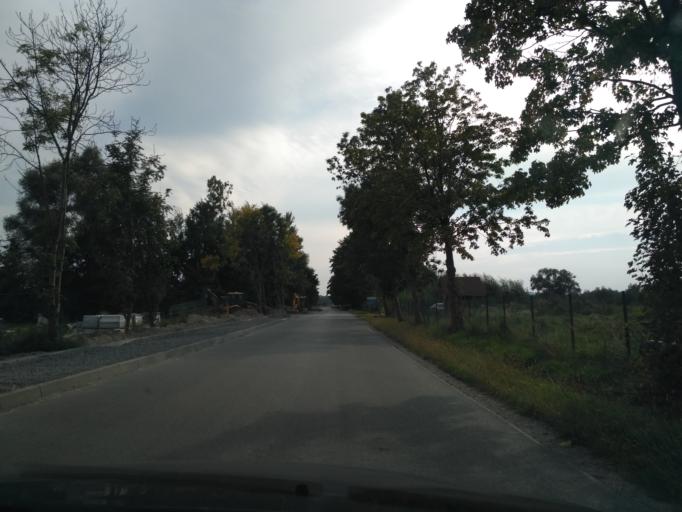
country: PL
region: Subcarpathian Voivodeship
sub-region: Powiat rzeszowski
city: Swilcza
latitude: 50.0895
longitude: 21.9169
